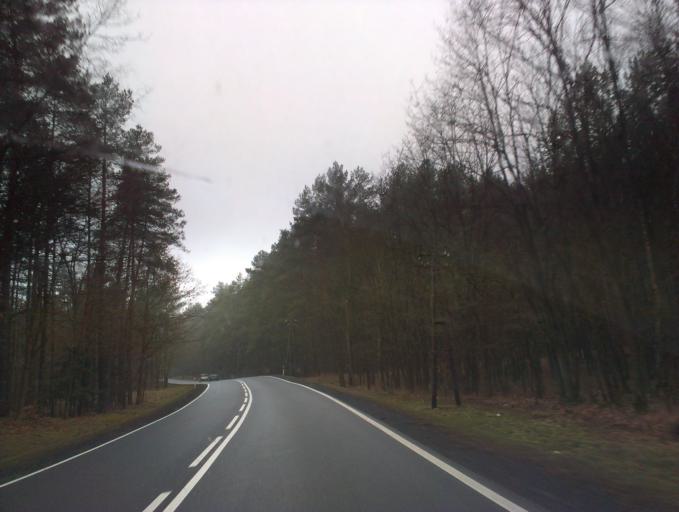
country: PL
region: Greater Poland Voivodeship
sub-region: Powiat zlotowski
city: Tarnowka
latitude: 53.2998
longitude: 16.7867
